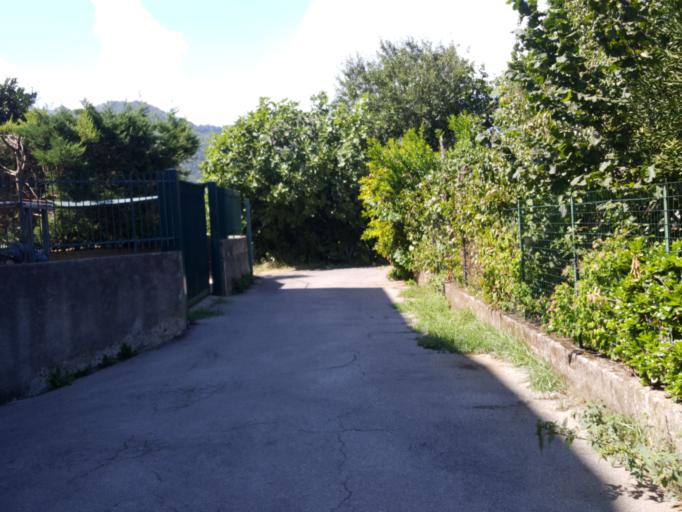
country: IT
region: Campania
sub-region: Provincia di Salerno
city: Baronissi
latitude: 40.7479
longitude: 14.7838
